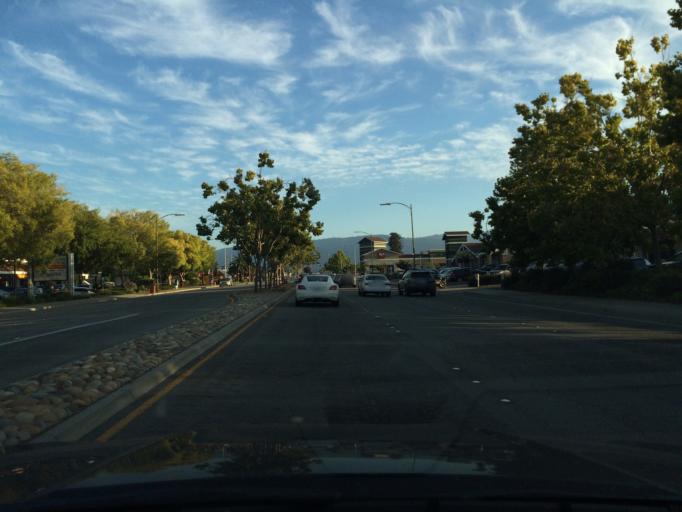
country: US
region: California
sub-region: Santa Clara County
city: Cupertino
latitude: 37.3059
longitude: -122.0323
